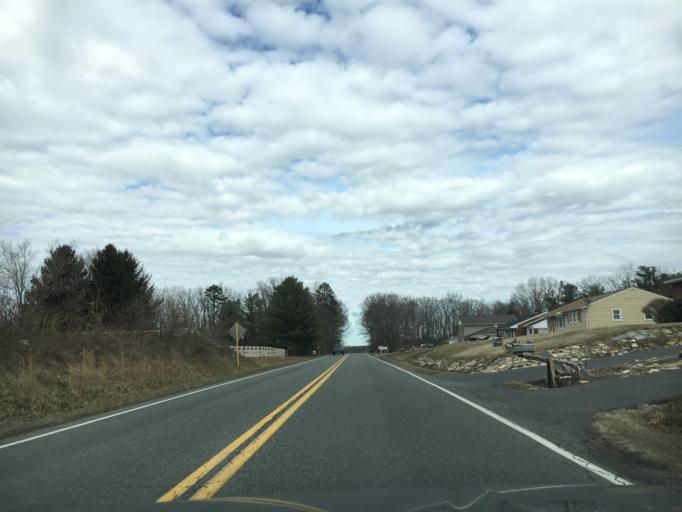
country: US
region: Virginia
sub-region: Augusta County
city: Crimora
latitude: 38.1309
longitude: -78.8455
